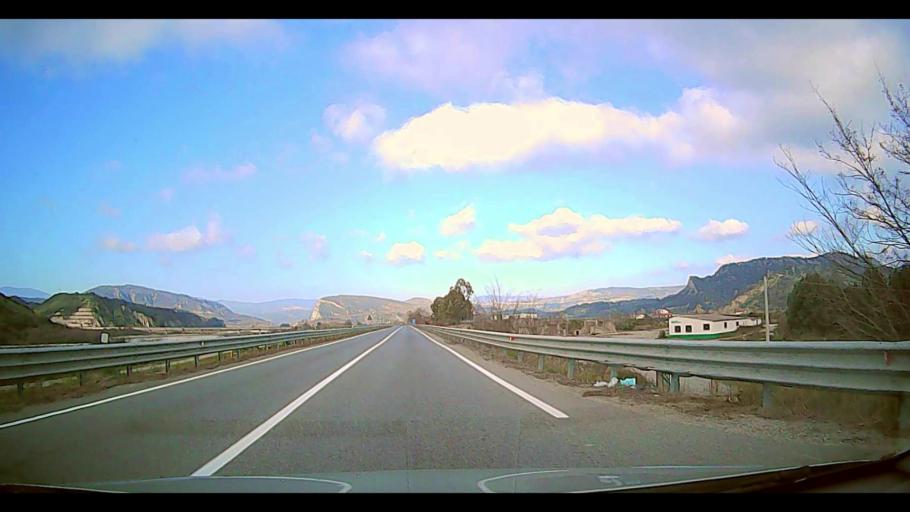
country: IT
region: Calabria
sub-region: Provincia di Crotone
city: Santa Severina
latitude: 39.1719
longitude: 16.9412
